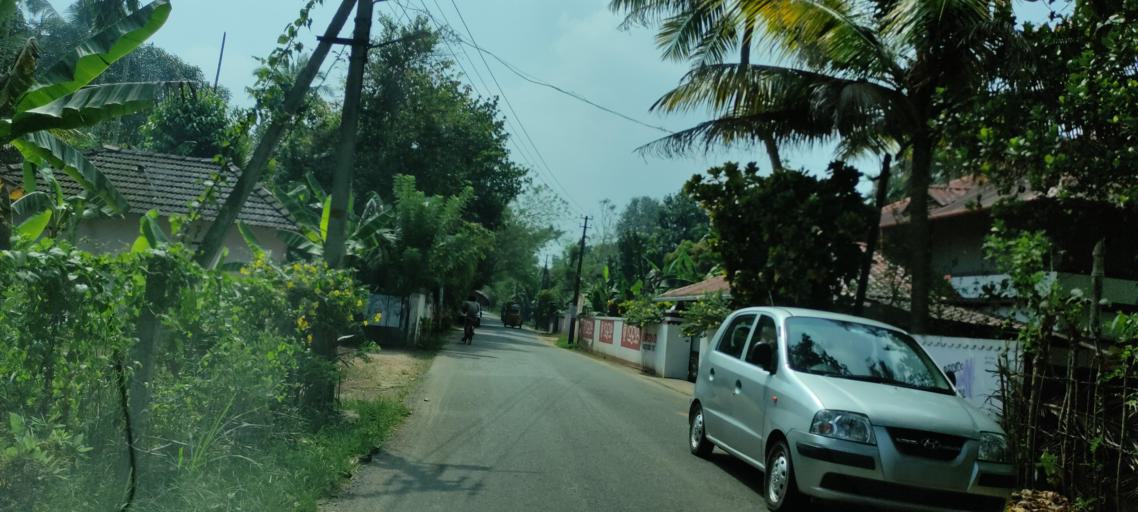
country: IN
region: Kerala
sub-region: Alappuzha
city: Shertallai
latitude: 9.6446
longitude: 76.3550
